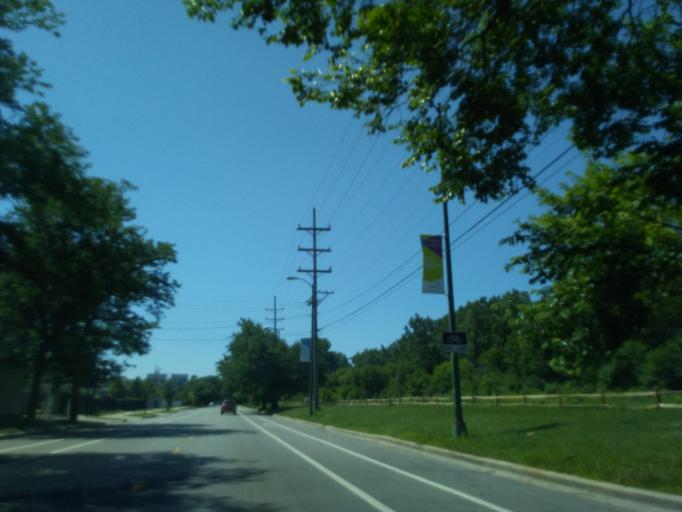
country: US
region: Illinois
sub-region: Cook County
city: Lincolnwood
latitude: 42.0038
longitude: -87.7094
